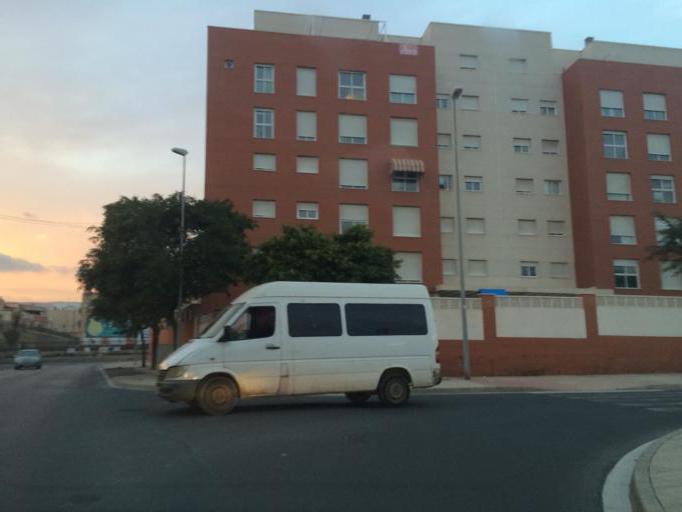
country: ES
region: Andalusia
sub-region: Provincia de Almeria
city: Almeria
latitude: 36.8443
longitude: -2.4364
